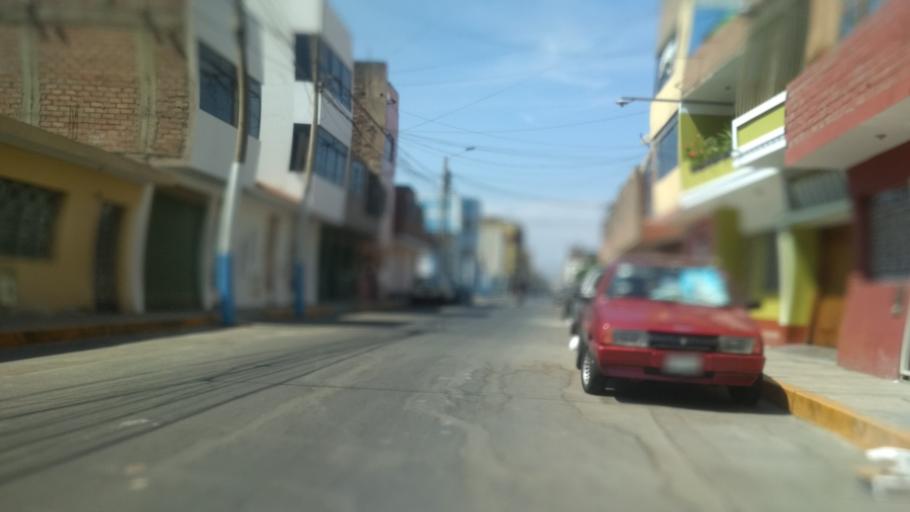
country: PE
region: Callao
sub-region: Callao
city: Callao
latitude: -12.0393
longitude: -77.0922
